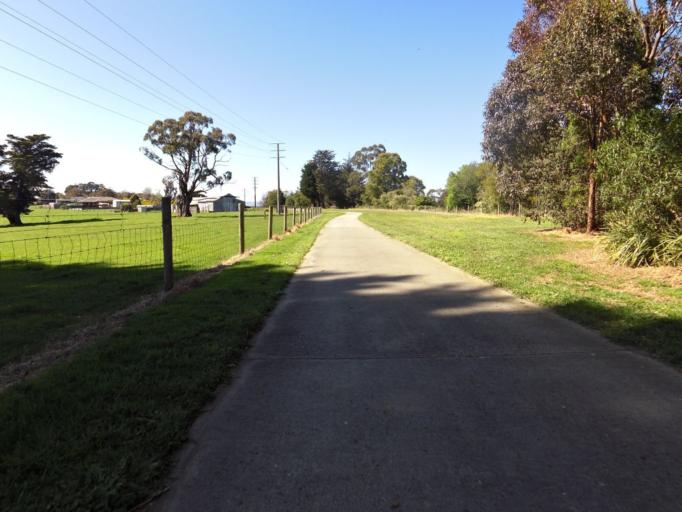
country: AU
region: Victoria
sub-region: Baw Baw
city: Warragul
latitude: -38.1405
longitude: 145.8863
